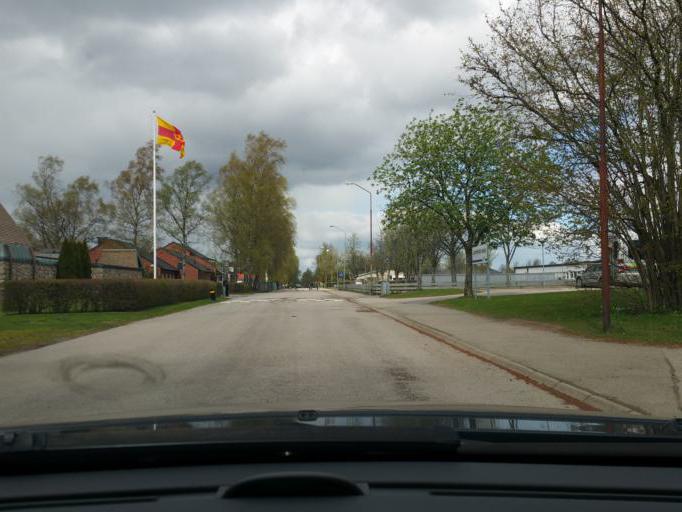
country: SE
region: Kronoberg
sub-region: Vaxjo Kommun
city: Lammhult
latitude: 57.1681
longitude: 14.5874
